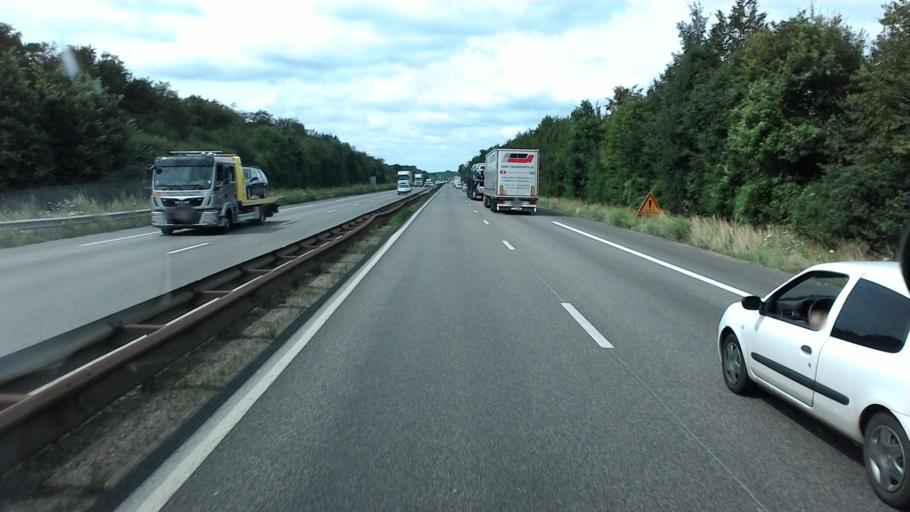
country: FR
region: Lorraine
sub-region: Departement de Meurthe-et-Moselle
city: Laxou
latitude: 48.6774
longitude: 6.1201
